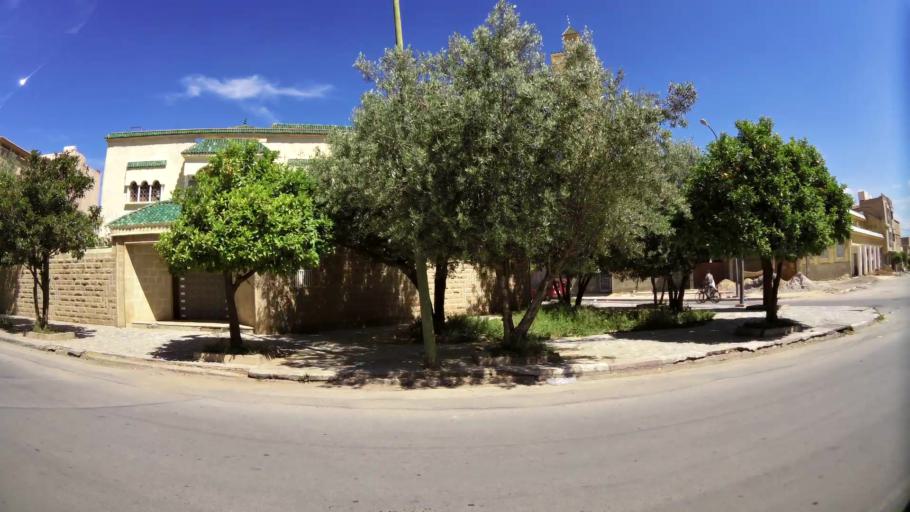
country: MA
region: Oriental
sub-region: Oujda-Angad
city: Oujda
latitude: 34.6656
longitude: -1.9299
